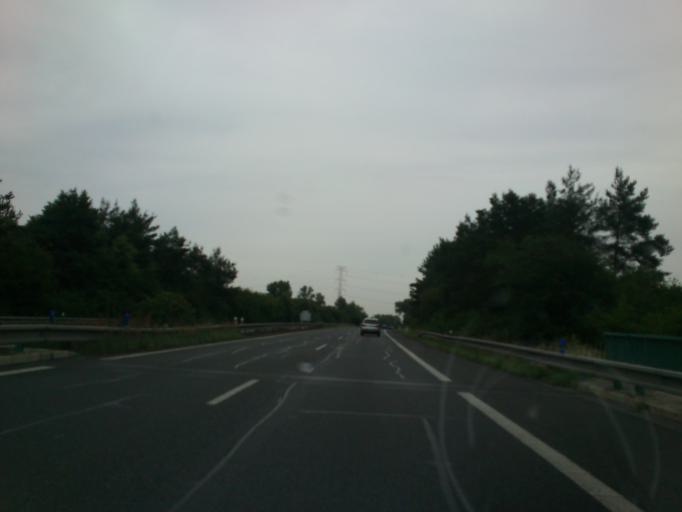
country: CZ
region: Central Bohemia
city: Benatky nad Jizerou
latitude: 50.2488
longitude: 14.7539
